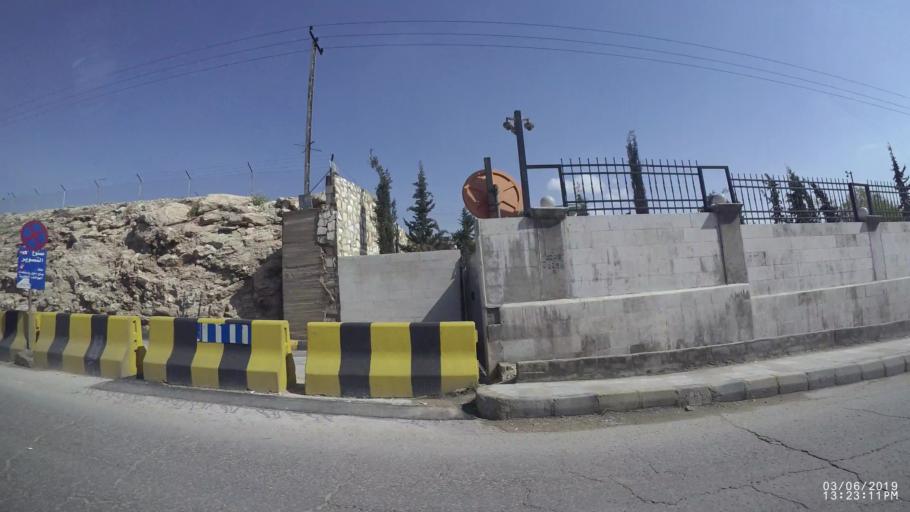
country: JO
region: Zarqa
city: Zarqa
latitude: 32.0537
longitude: 36.0944
